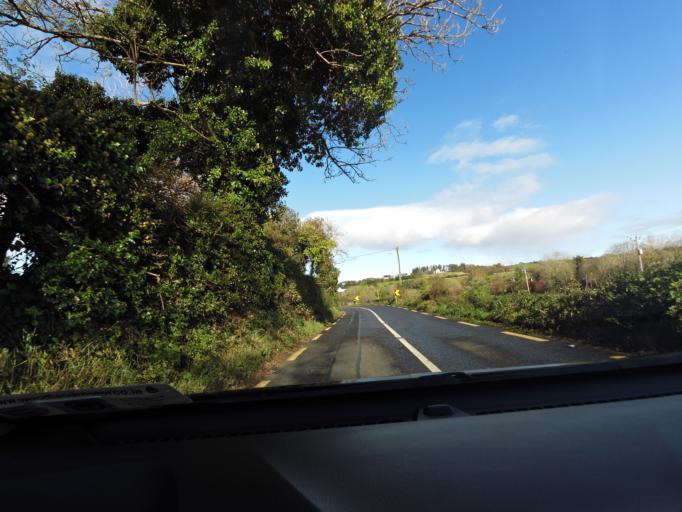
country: IE
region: Connaught
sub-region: Maigh Eo
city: Westport
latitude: 53.8089
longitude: -9.5287
